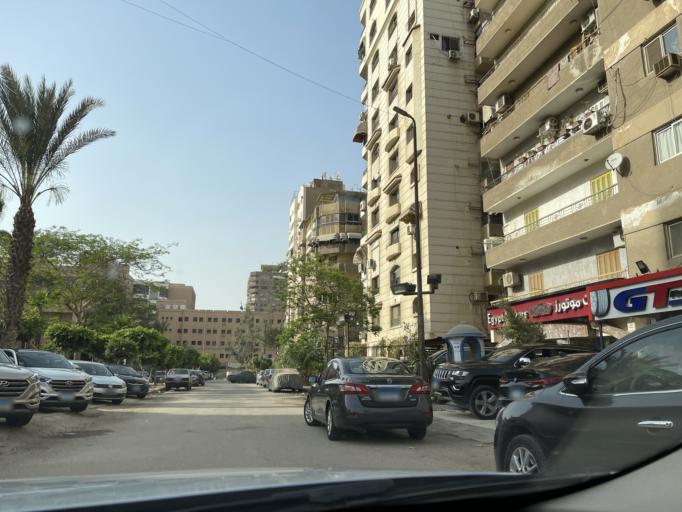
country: EG
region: Muhafazat al Qahirah
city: Cairo
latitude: 30.0661
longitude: 31.3530
